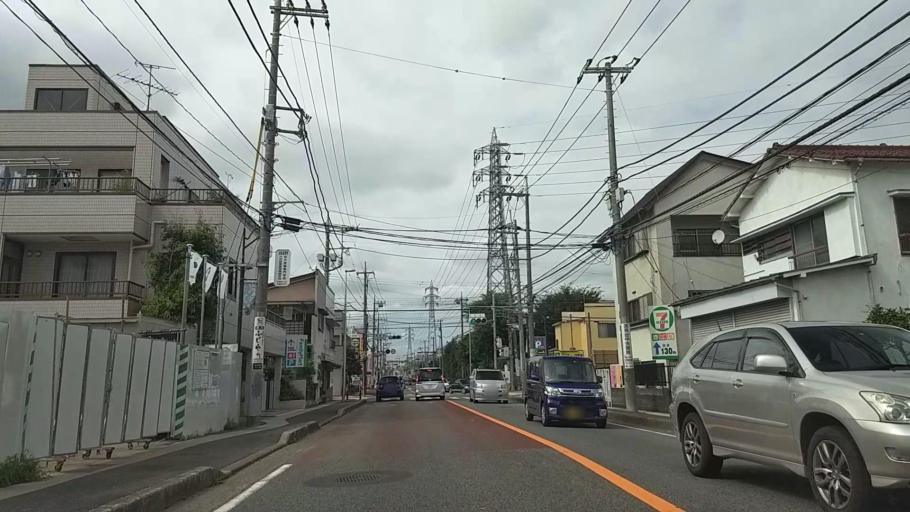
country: JP
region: Kanagawa
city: Minami-rinkan
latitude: 35.4708
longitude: 139.4658
